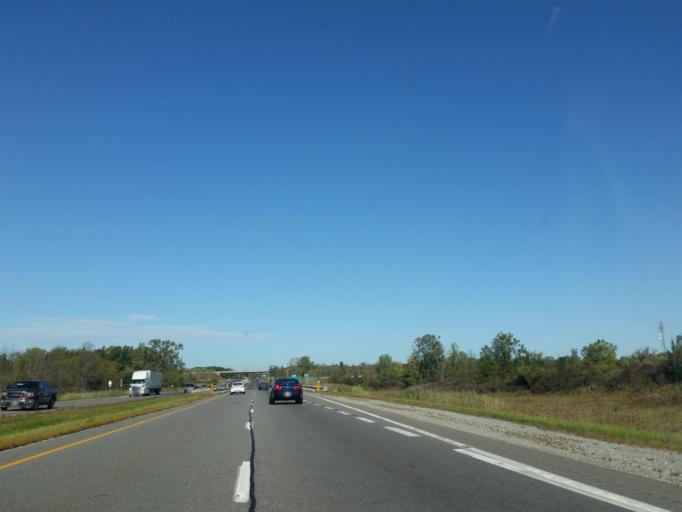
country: CA
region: Ontario
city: Niagara Falls
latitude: 43.0274
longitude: -79.1058
